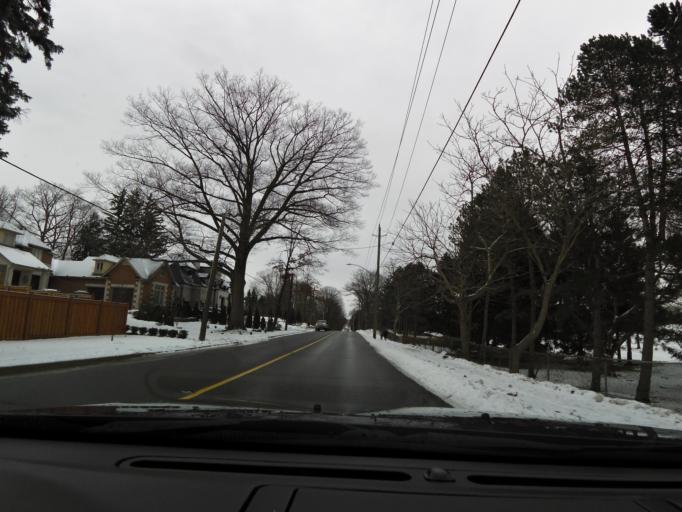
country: CA
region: Ontario
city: Ancaster
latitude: 43.2215
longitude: -79.9769
